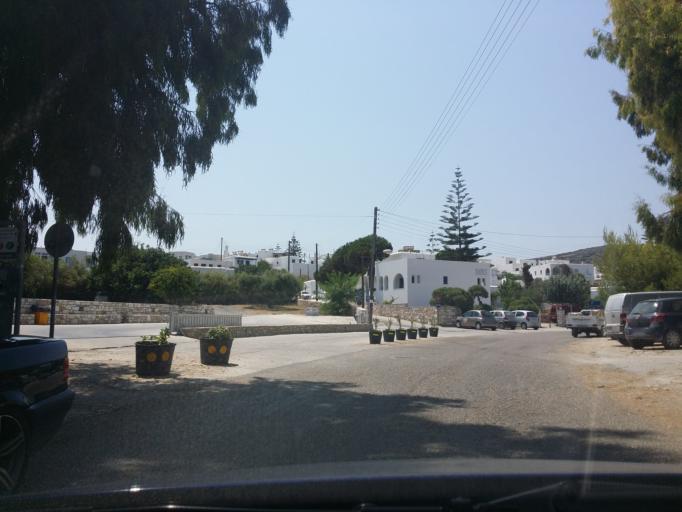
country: GR
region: South Aegean
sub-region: Nomos Kykladon
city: Naousa
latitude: 37.1216
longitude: 25.2385
